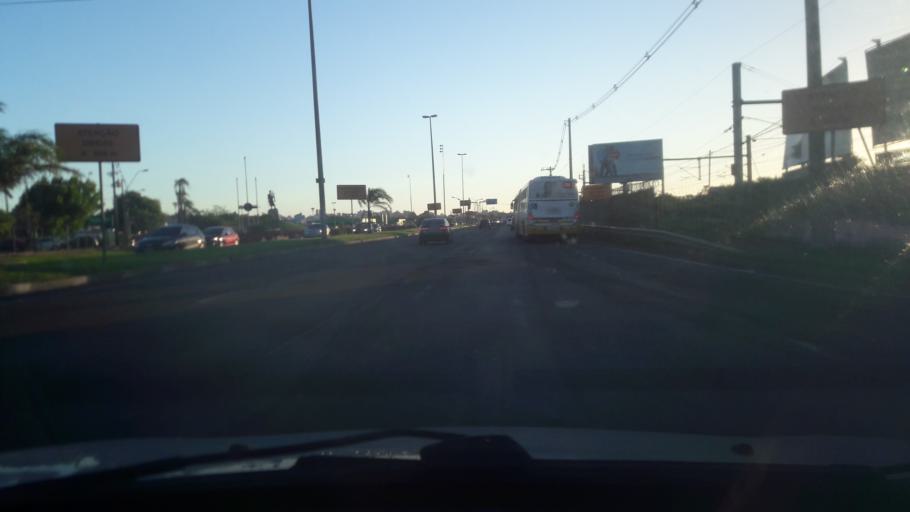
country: BR
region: Rio Grande do Sul
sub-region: Porto Alegre
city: Porto Alegre
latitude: -29.9898
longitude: -51.1838
